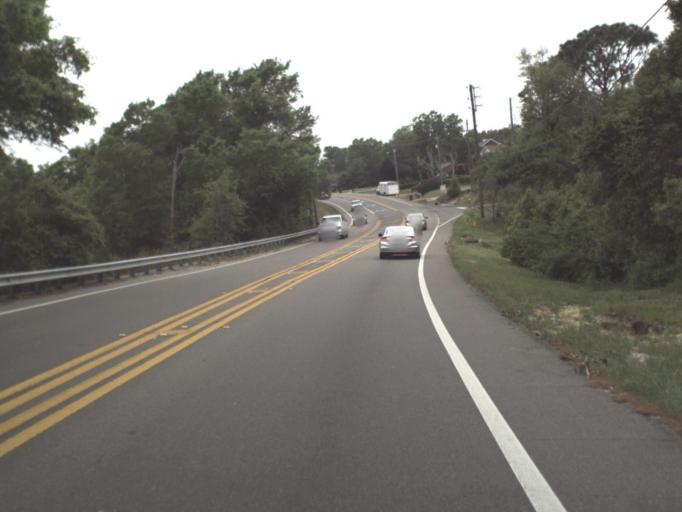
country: US
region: Florida
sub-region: Escambia County
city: East Pensacola Heights
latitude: 30.4590
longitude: -87.1662
